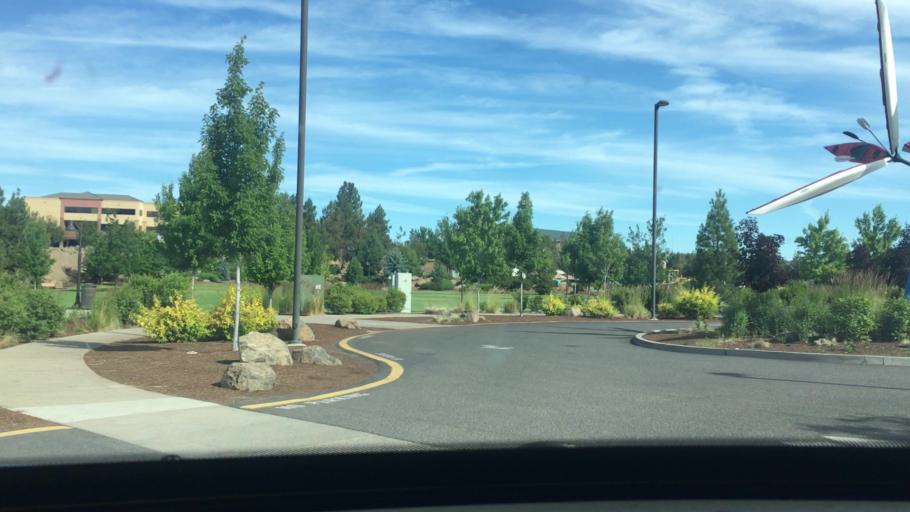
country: US
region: Oregon
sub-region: Deschutes County
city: Bend
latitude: 44.0428
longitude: -121.3208
